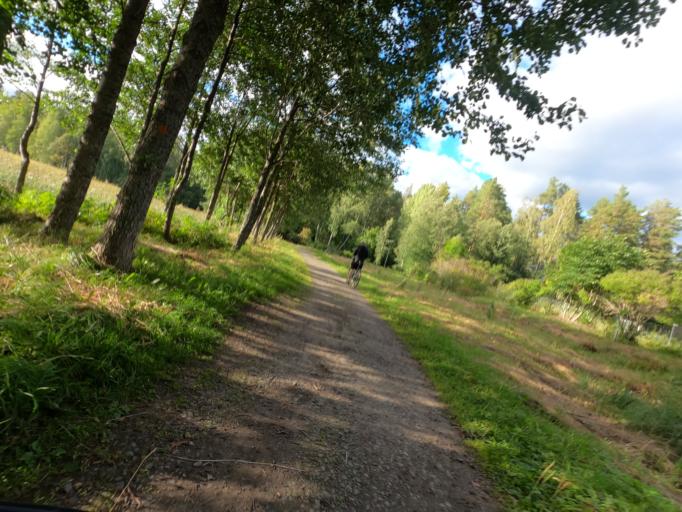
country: FI
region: North Karelia
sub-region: Joensuu
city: Joensuu
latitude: 62.6019
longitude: 29.7215
